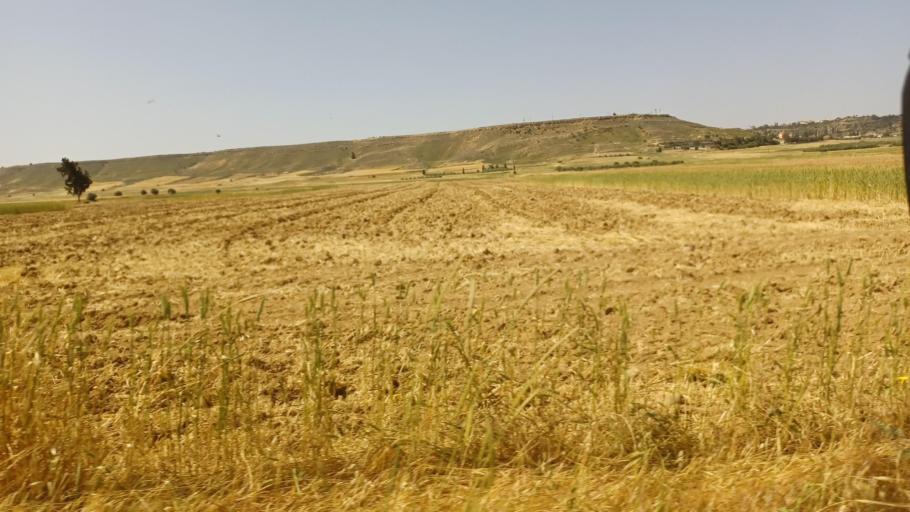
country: CY
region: Lefkosia
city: Mammari
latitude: 35.1835
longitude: 33.2189
